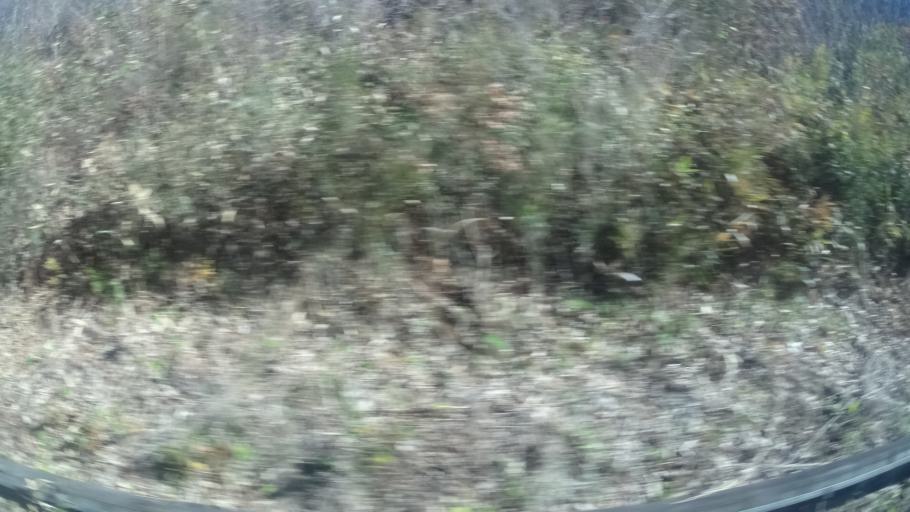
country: JP
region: Fukushima
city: Namie
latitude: 37.6775
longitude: 140.9715
